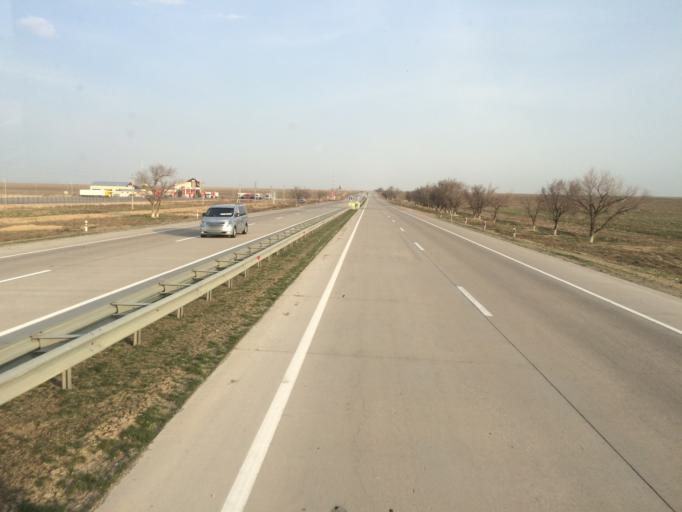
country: KZ
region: Ongtustik Qazaqstan
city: Temirlanovka
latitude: 42.8423
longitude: 69.1019
